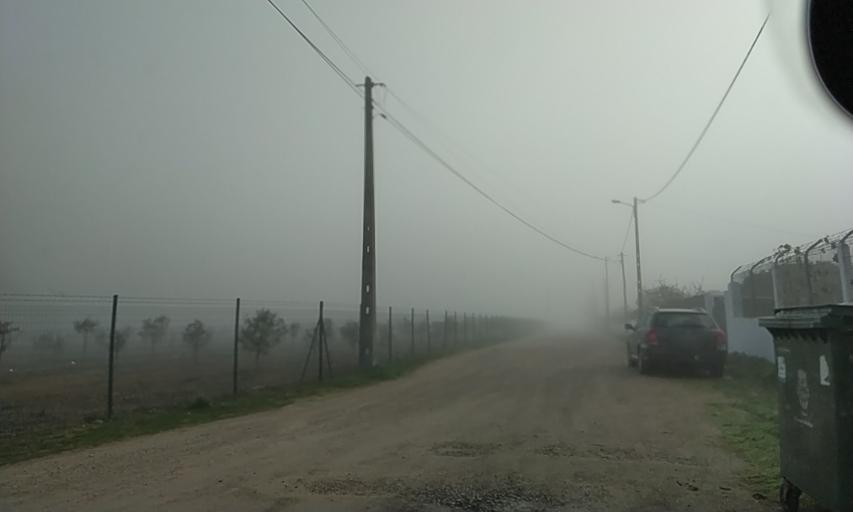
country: PT
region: Setubal
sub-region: Palmela
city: Pinhal Novo
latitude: 38.6141
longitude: -8.8938
